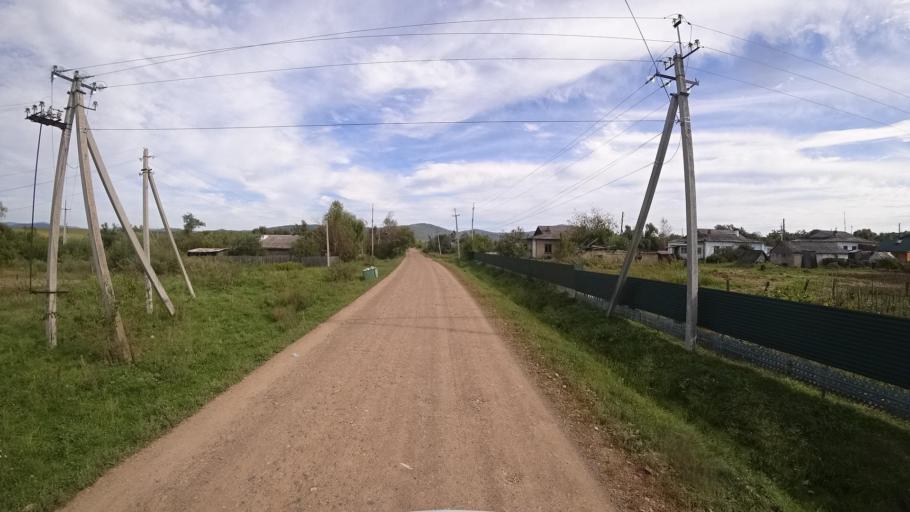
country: RU
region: Primorskiy
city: Dostoyevka
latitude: 44.3075
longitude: 133.4556
